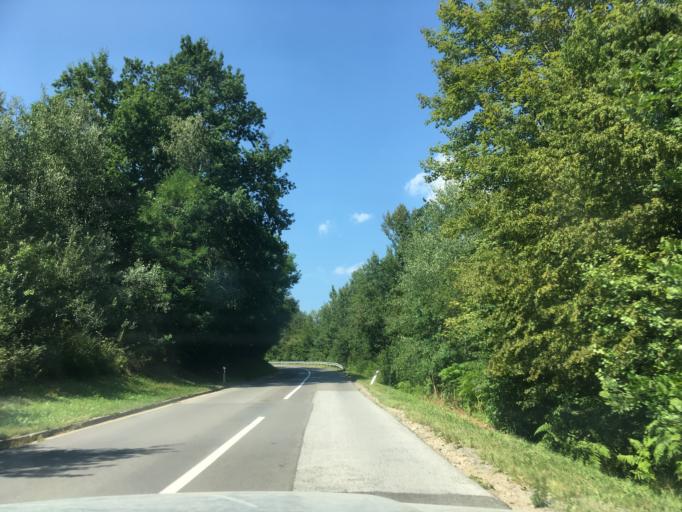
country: HR
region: Karlovacka
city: Ozalj
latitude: 45.5205
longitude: 15.3938
